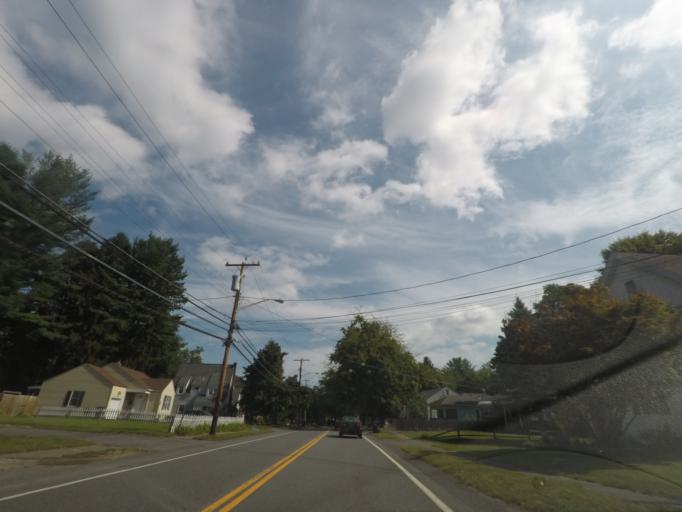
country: US
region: New York
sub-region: Albany County
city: Delmar
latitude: 42.6237
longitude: -73.8464
